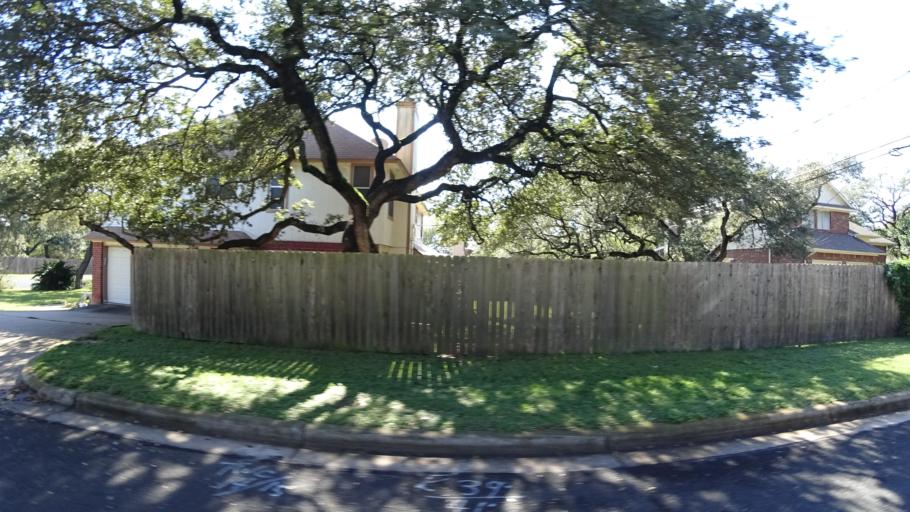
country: US
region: Texas
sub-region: Travis County
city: Shady Hollow
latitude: 30.2161
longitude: -97.8722
